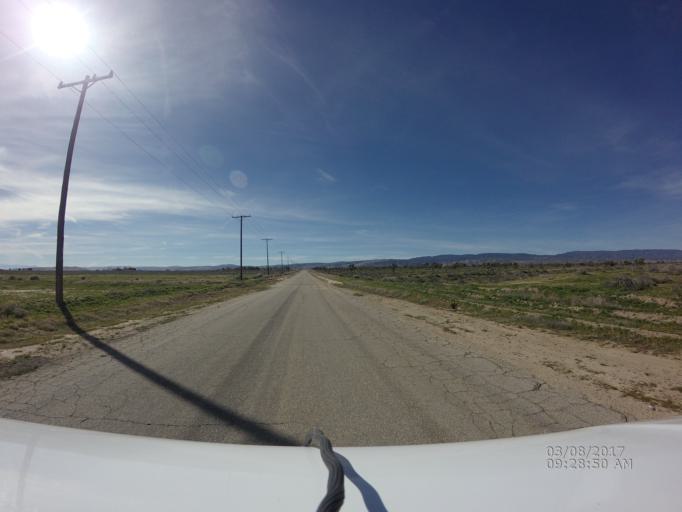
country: US
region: California
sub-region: Los Angeles County
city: Green Valley
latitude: 34.8032
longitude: -118.4667
